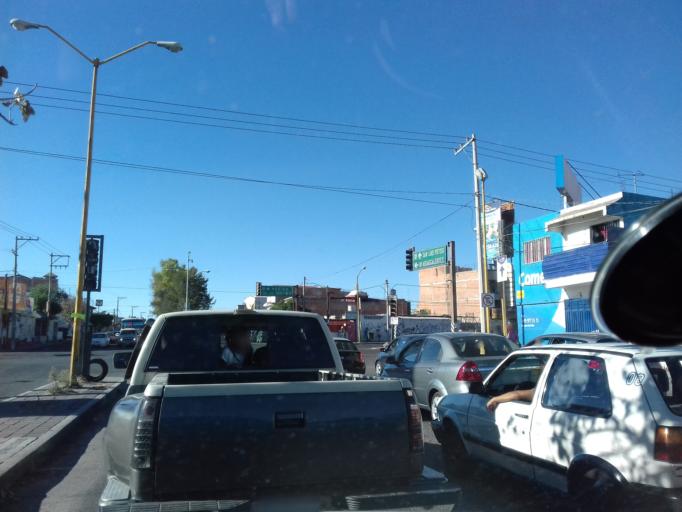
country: MX
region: Aguascalientes
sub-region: Aguascalientes
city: San Sebastian [Fraccionamiento]
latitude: 21.8517
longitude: -102.2693
